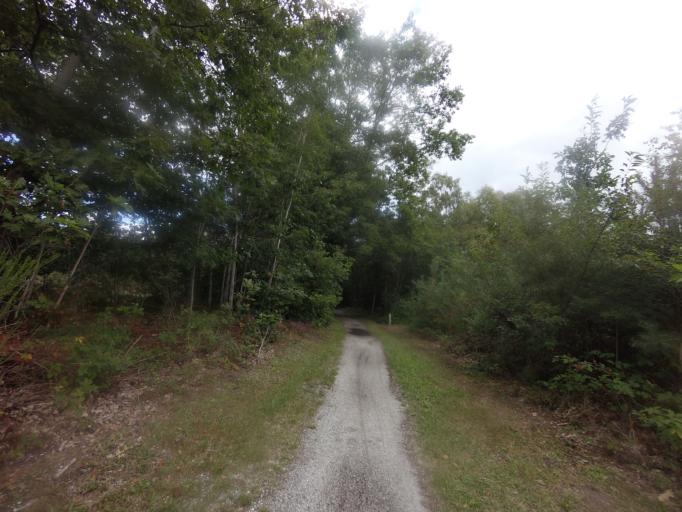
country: NL
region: Overijssel
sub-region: Gemeente Staphorst
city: Staphorst
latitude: 52.6371
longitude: 6.2726
